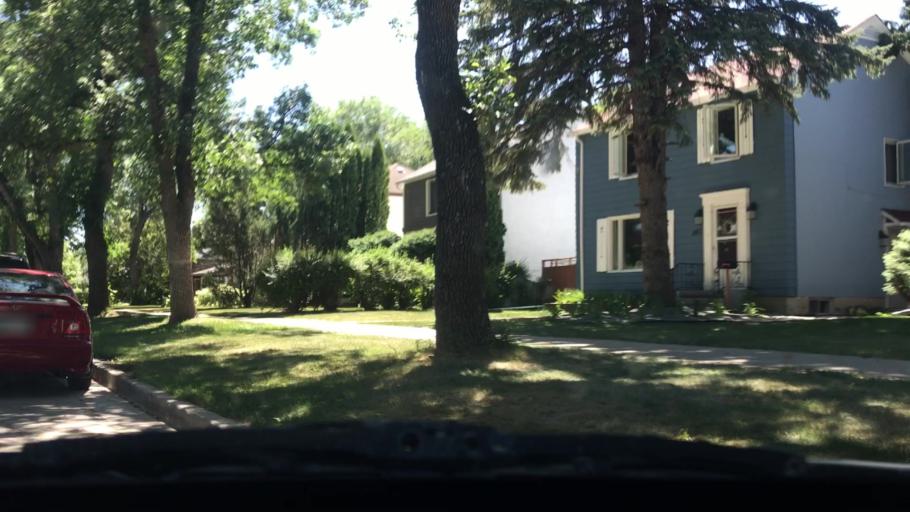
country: CA
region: Manitoba
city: Winnipeg
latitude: 49.8693
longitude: -97.1961
